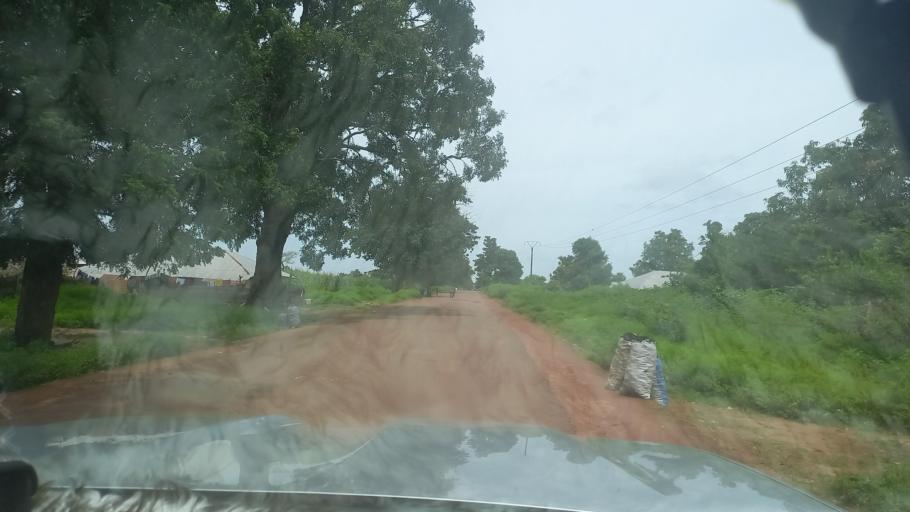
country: SN
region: Kolda
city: Marsassoum
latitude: 12.9170
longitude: -16.0096
